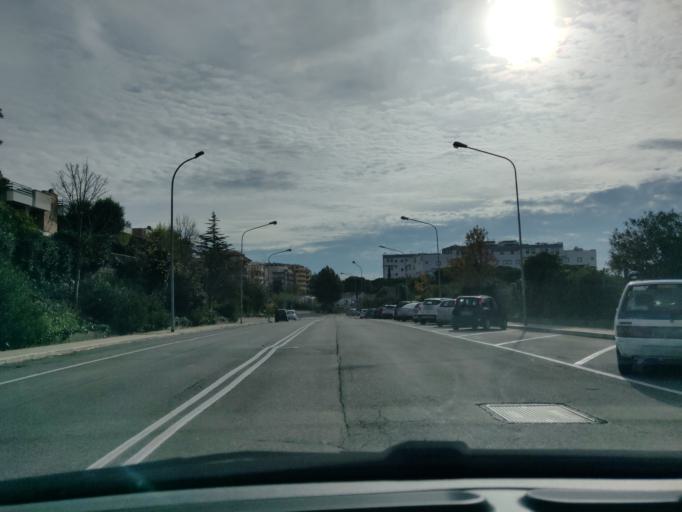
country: IT
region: Latium
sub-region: Citta metropolitana di Roma Capitale
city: Civitavecchia
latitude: 42.1001
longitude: 11.8092
